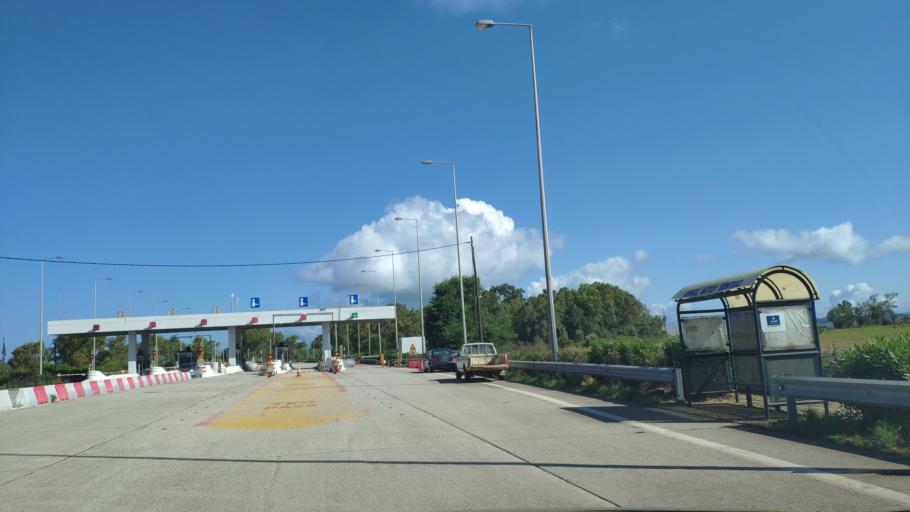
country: GR
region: Epirus
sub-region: Nomos Prevezis
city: Preveza
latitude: 38.9393
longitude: 20.7668
